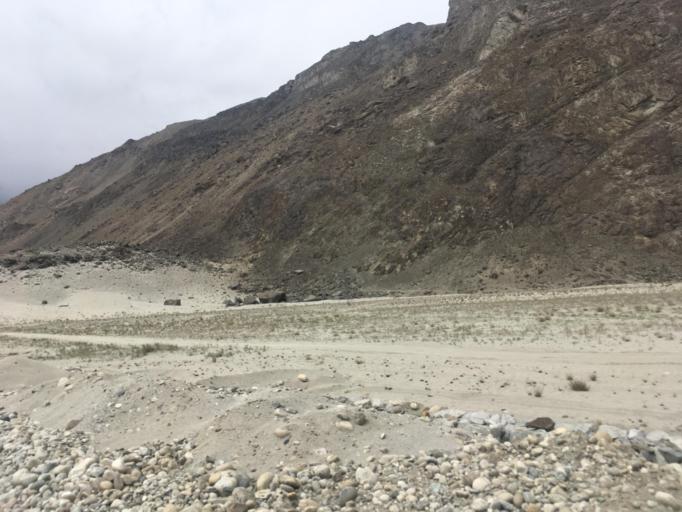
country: PK
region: Gilgit-Baltistan
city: Skardu
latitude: 35.3150
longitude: 75.6575
